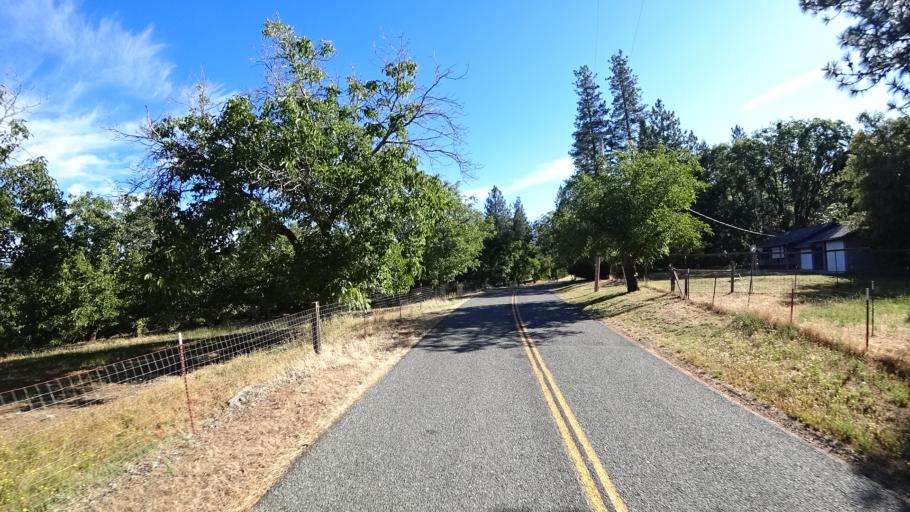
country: US
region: California
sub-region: Amador County
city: Pioneer
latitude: 38.3873
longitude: -120.5495
